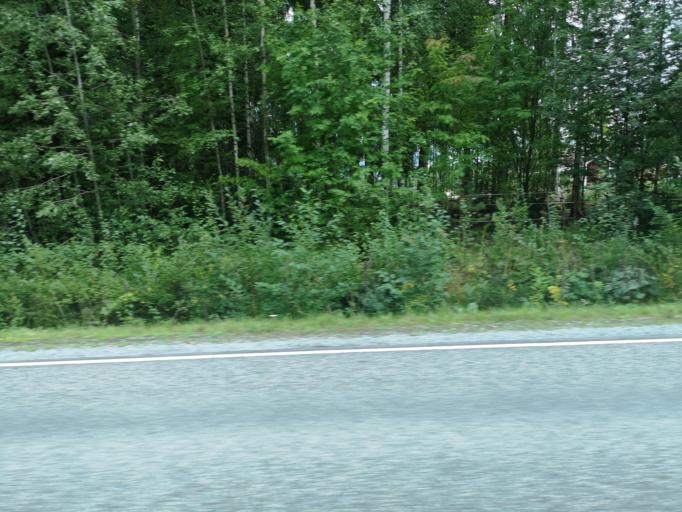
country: FI
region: Central Finland
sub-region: Jyvaeskylae
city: Hankasalmi
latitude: 62.3717
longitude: 26.4425
